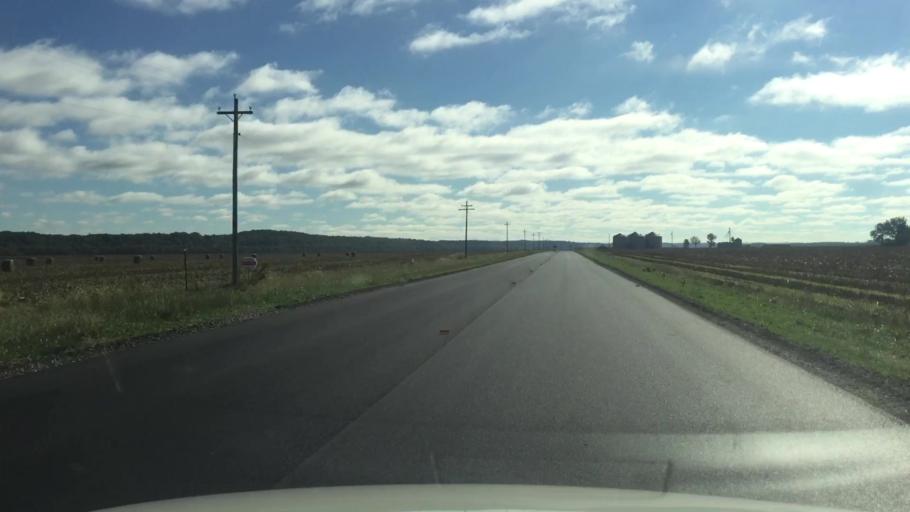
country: US
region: Missouri
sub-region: Howard County
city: New Franklin
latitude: 39.0023
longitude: -92.6890
